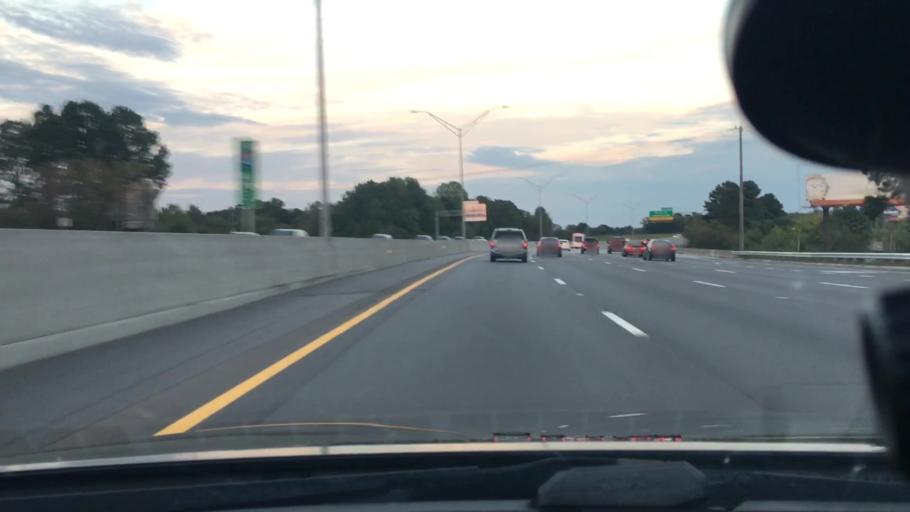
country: US
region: North Carolina
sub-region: Wake County
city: Raleigh
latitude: 35.7541
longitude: -78.6428
